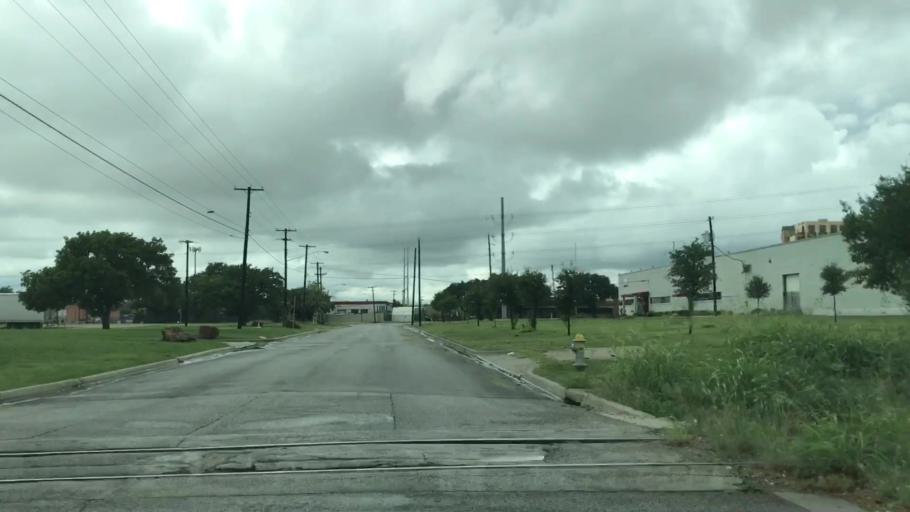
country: US
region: Texas
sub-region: Dallas County
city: Irving
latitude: 32.8245
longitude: -96.8866
